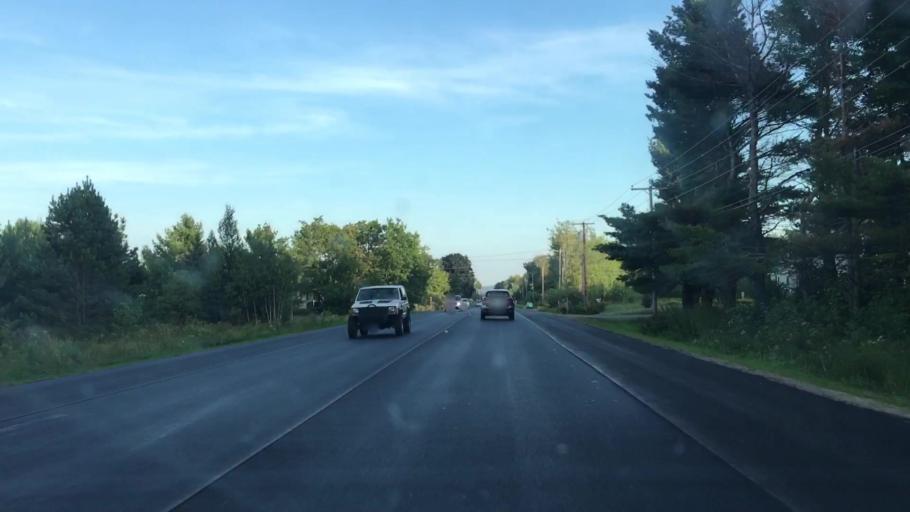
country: US
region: Maine
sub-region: Penobscot County
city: Hampden
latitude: 44.7617
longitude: -68.8488
